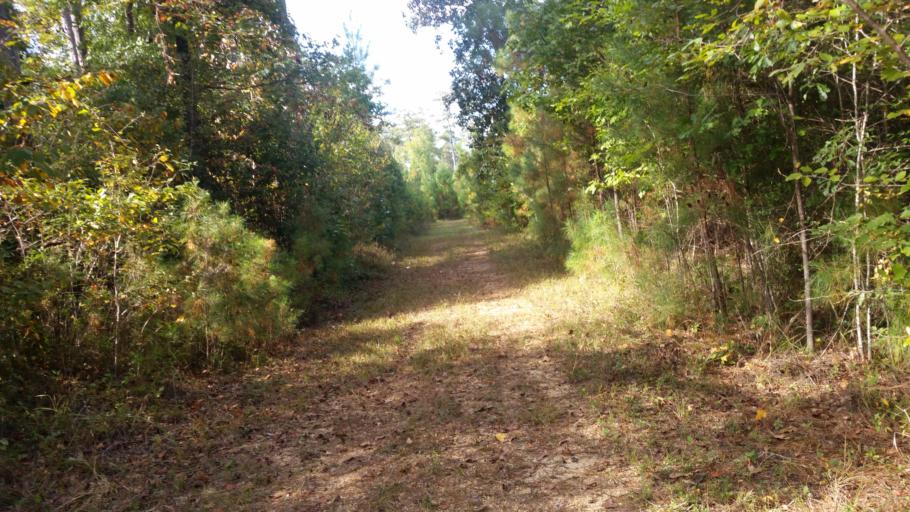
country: US
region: Mississippi
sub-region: Stone County
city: Wiggins
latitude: 30.9940
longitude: -89.0552
